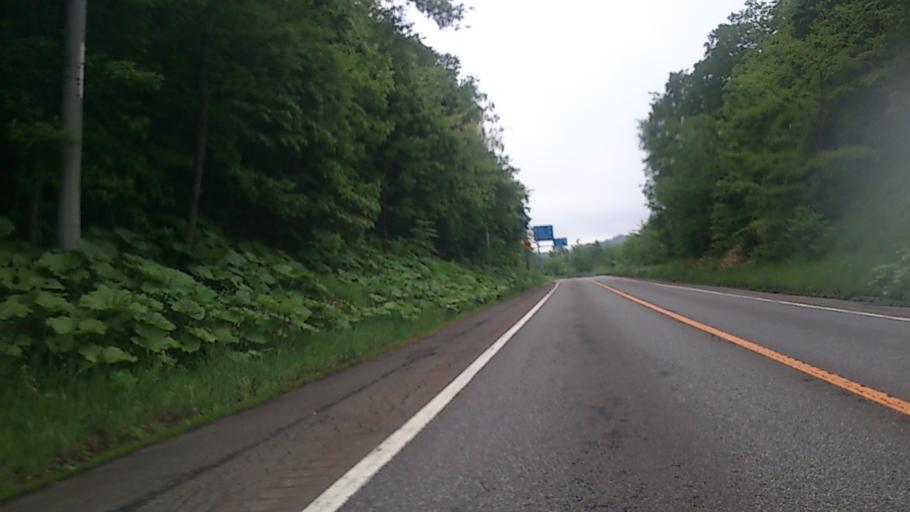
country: JP
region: Hokkaido
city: Obihiro
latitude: 42.8327
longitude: 143.7654
